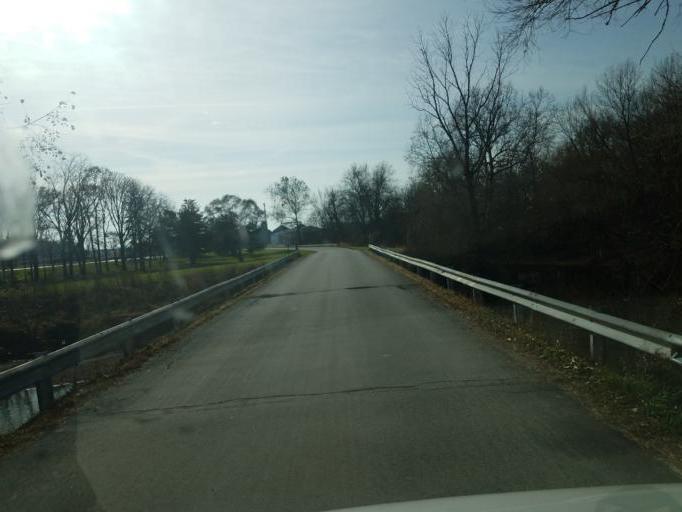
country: US
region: Ohio
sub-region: Hardin County
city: Kenton
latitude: 40.6093
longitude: -83.4388
